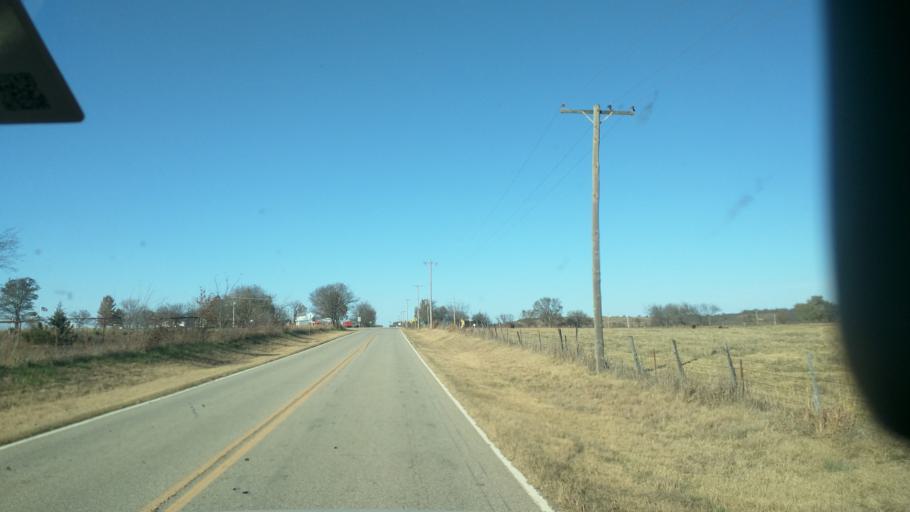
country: US
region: Oklahoma
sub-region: Nowata County
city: Nowata
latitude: 36.7692
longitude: -95.5396
